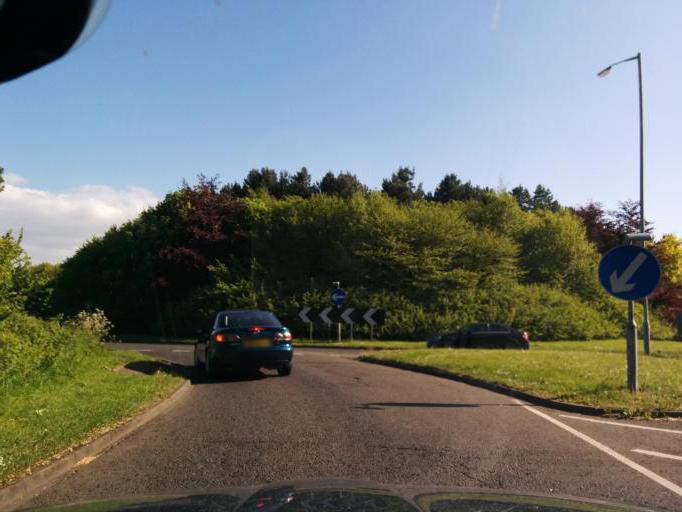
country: GB
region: England
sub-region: Northumberland
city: Cramlington
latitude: 55.0966
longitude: -1.5955
